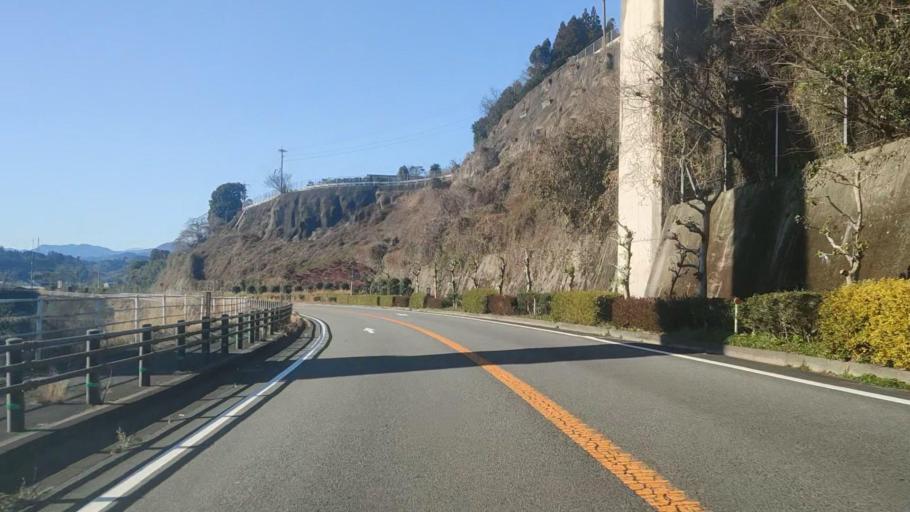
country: JP
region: Oita
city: Usuki
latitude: 33.0695
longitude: 131.6490
